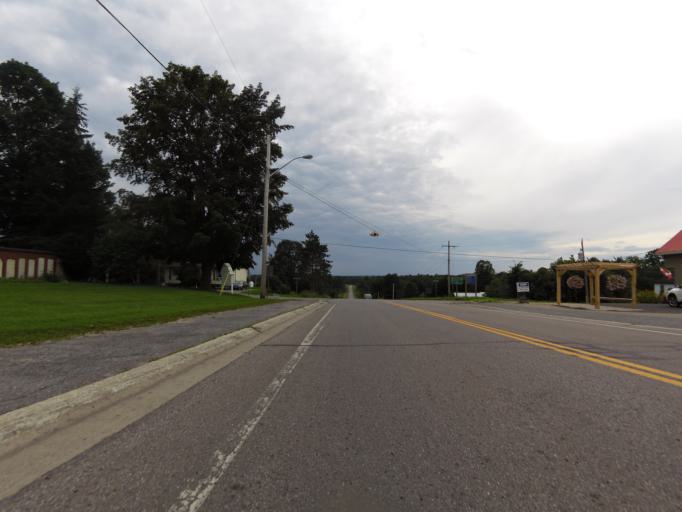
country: CA
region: Ontario
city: Perth
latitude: 45.0979
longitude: -76.3959
